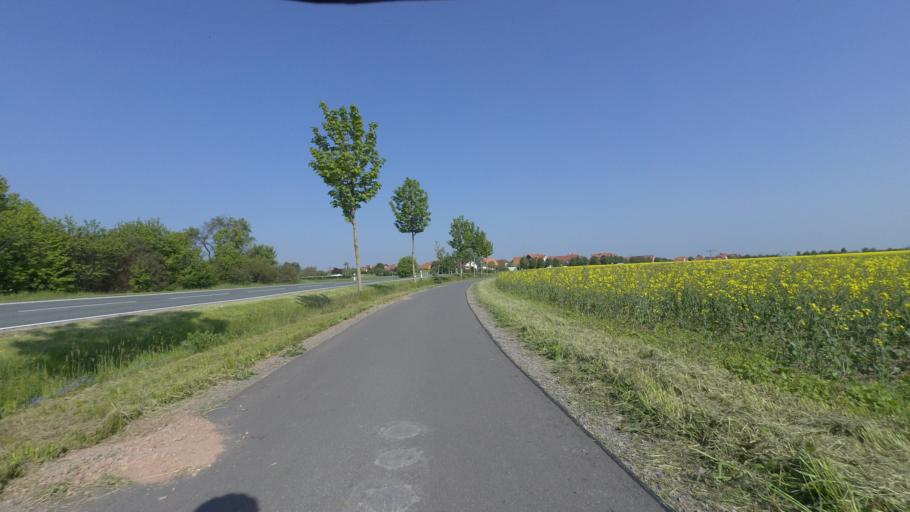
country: DE
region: Saxony-Anhalt
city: Darlingerode
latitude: 51.8470
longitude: 10.7433
